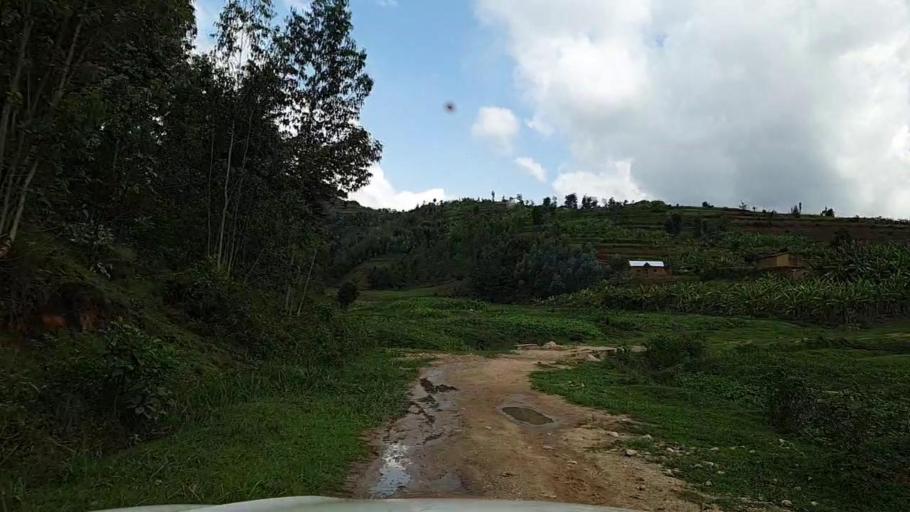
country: RW
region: Southern Province
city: Gikongoro
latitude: -2.3908
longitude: 29.5503
